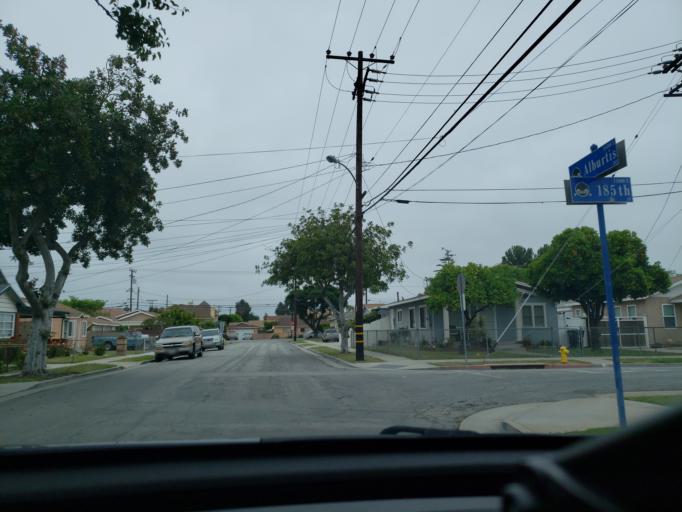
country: US
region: California
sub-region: Los Angeles County
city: Artesia
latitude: 33.8637
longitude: -118.0844
